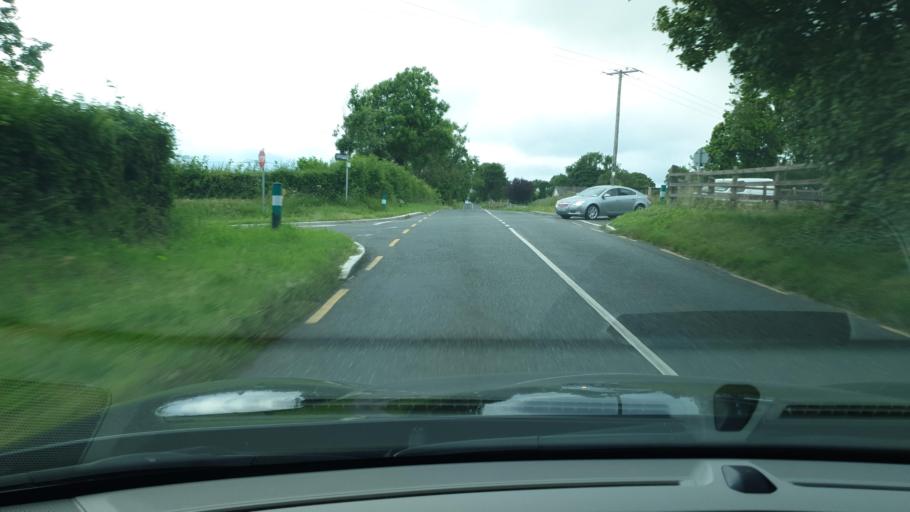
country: IE
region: Leinster
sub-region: An Mhi
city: Ratoath
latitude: 53.5257
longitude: -6.4818
